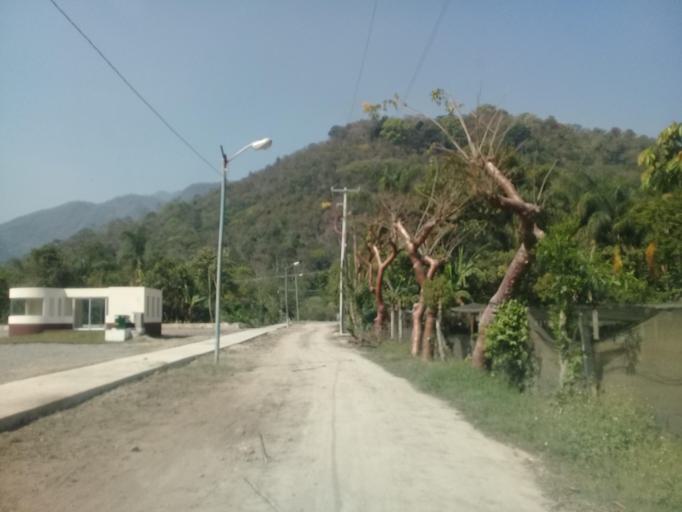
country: MX
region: Veracruz
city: Rafael Delgado
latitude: 18.7942
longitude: -97.0067
